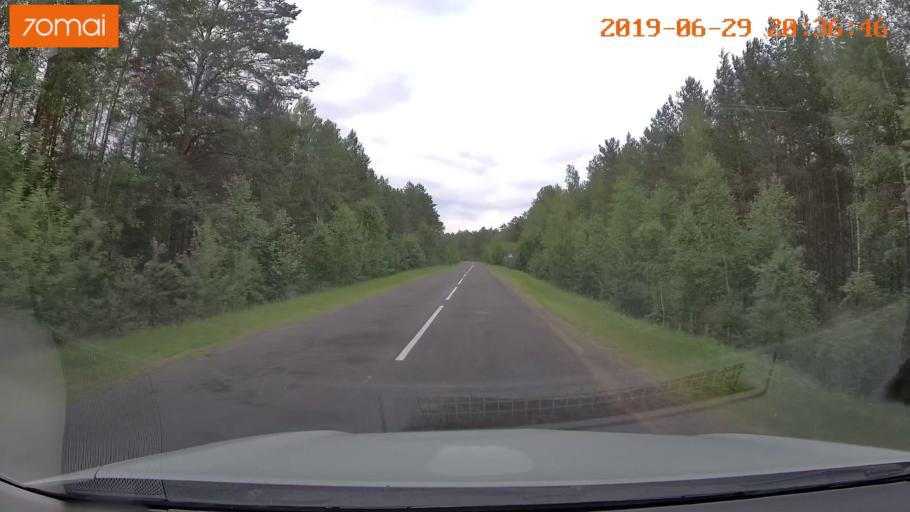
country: BY
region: Brest
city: Hantsavichy
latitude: 52.5299
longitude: 26.3611
